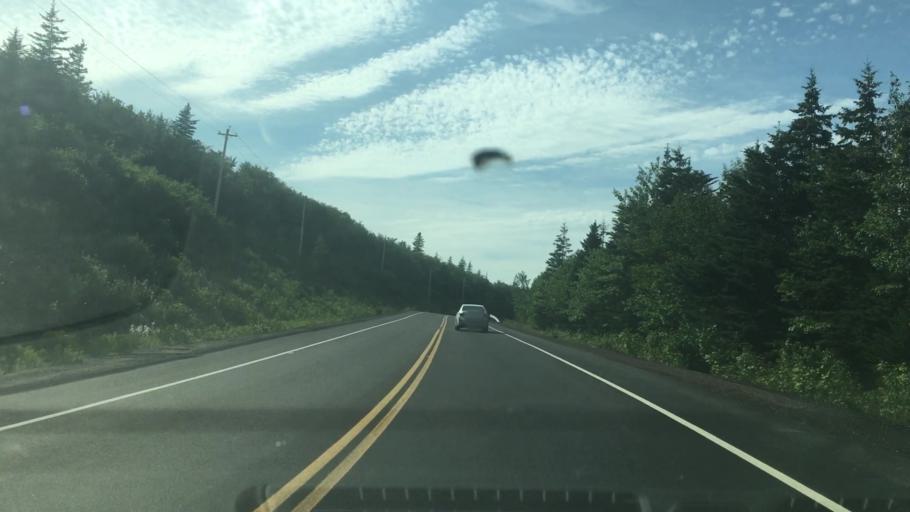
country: CA
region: Nova Scotia
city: Sydney Mines
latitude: 46.8369
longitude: -60.3811
